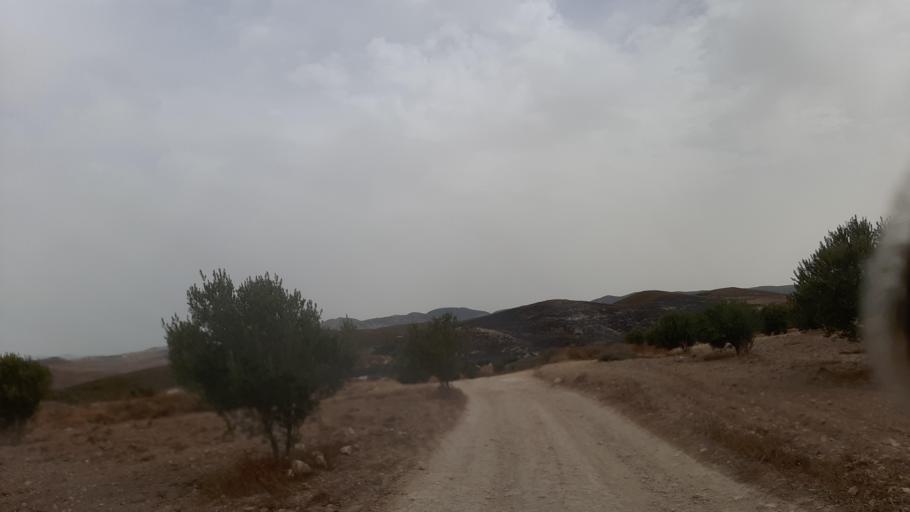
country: TN
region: Tunis
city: La Mohammedia
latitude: 36.5655
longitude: 10.1480
